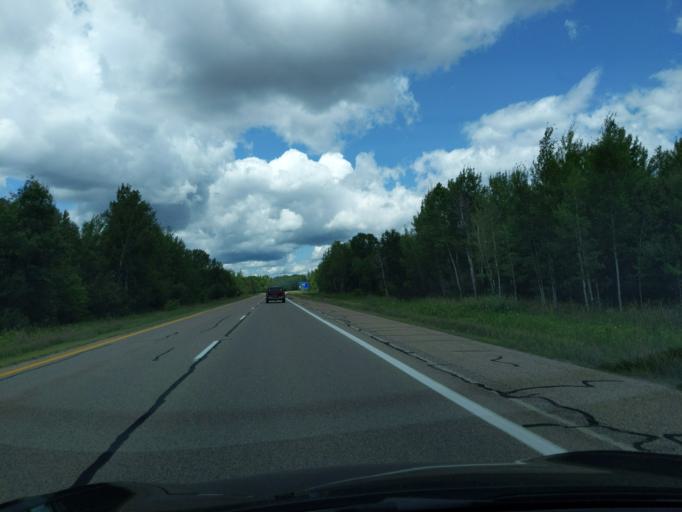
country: US
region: Michigan
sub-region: Roscommon County
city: Houghton Lake
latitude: 44.3063
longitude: -84.8035
